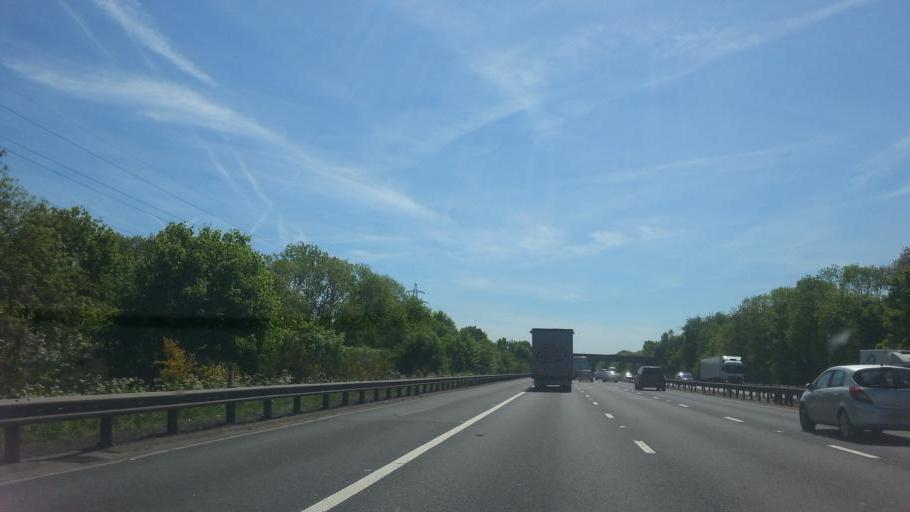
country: GB
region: England
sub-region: Central Bedfordshire
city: Steppingley
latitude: 51.9962
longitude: -0.5391
